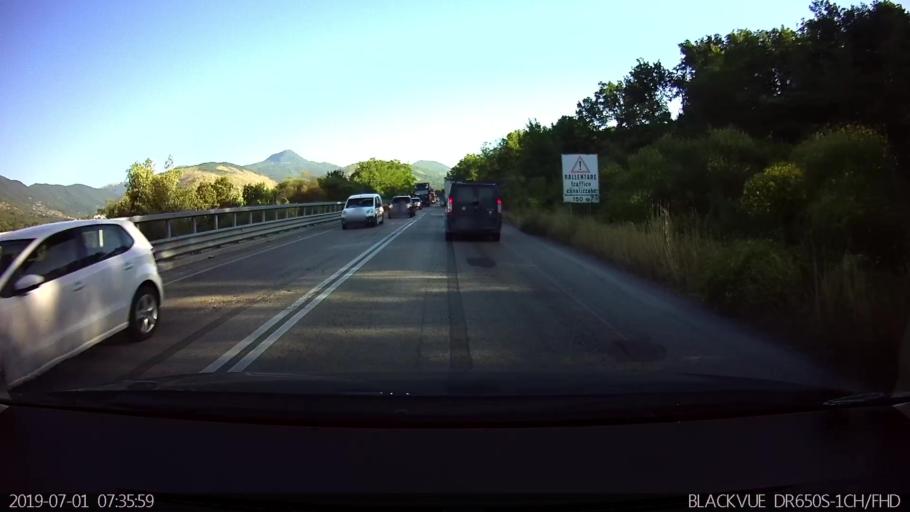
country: IT
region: Latium
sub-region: Provincia di Latina
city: Prossedi
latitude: 41.5283
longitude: 13.2683
